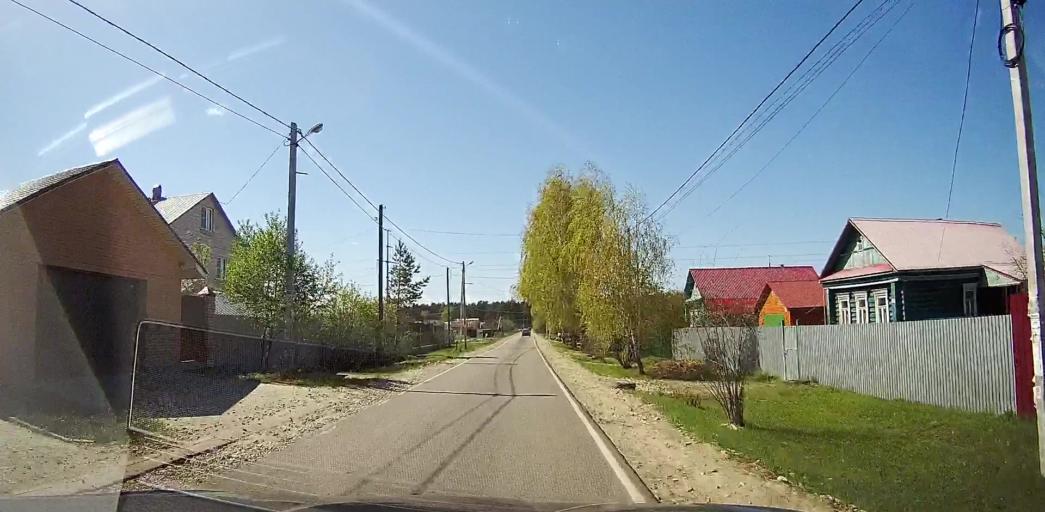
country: RU
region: Moskovskaya
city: Malyshevo
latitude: 55.4622
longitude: 38.3401
